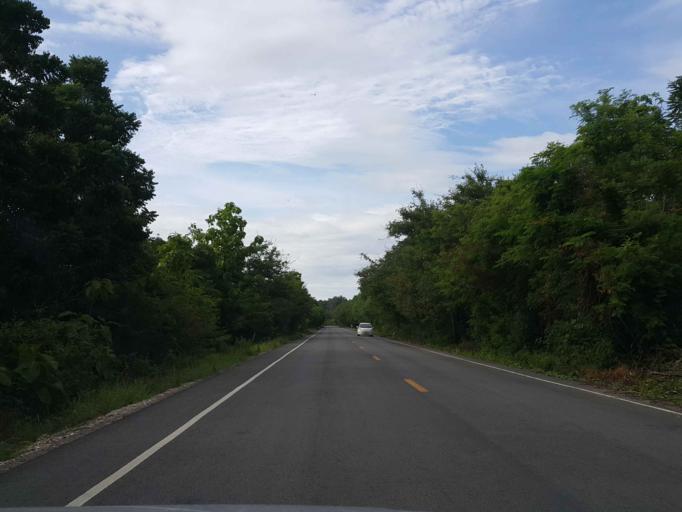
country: TH
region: Sukhothai
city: Thung Saliam
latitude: 17.2869
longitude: 99.5270
